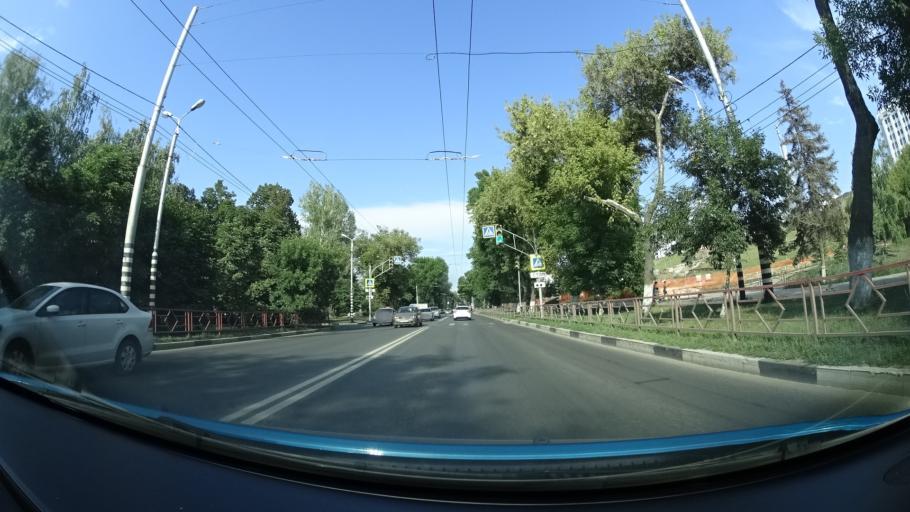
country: RU
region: Samara
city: Samara
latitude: 53.2041
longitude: 50.1063
